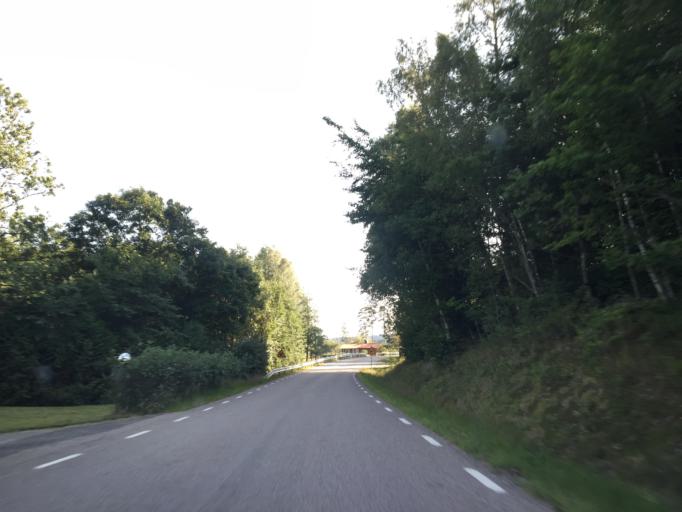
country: SE
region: Vaestra Goetaland
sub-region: Lilla Edets Kommun
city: Lilla Edet
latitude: 58.1708
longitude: 12.0813
